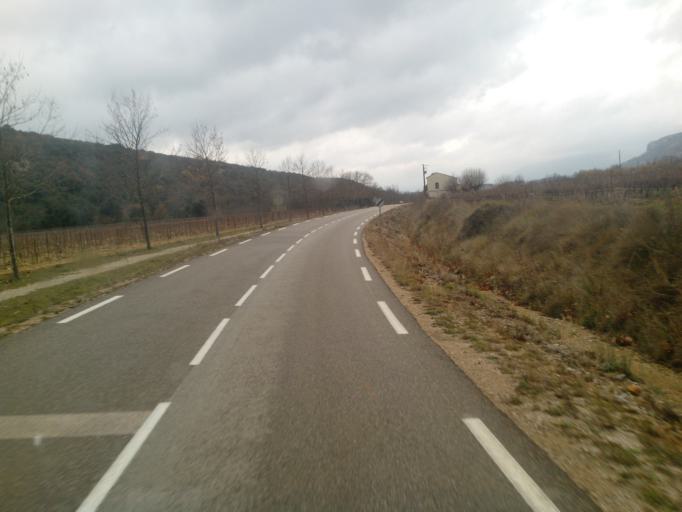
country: FR
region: Languedoc-Roussillon
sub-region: Departement de l'Herault
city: Saint-Bauzille-de-Putois
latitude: 43.9222
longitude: 3.7904
